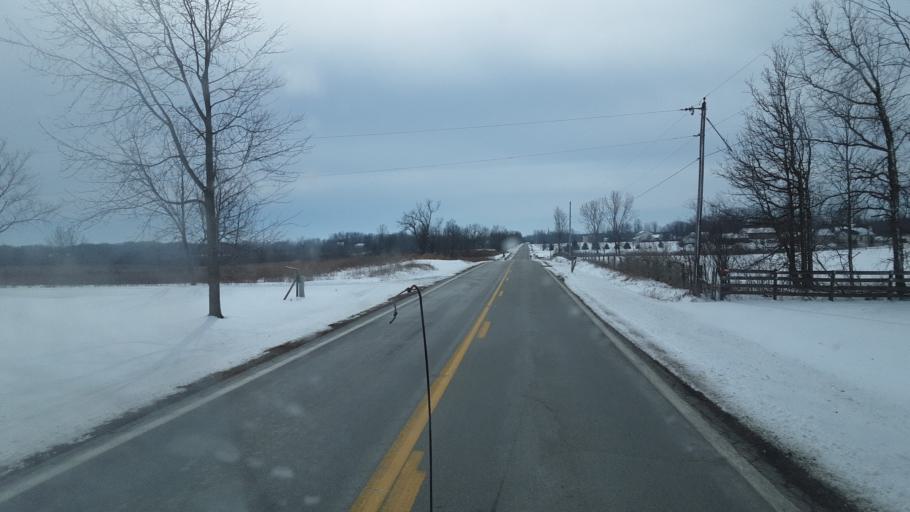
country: US
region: Ohio
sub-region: Madison County
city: Choctaw Lake
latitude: 39.9681
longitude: -83.5024
